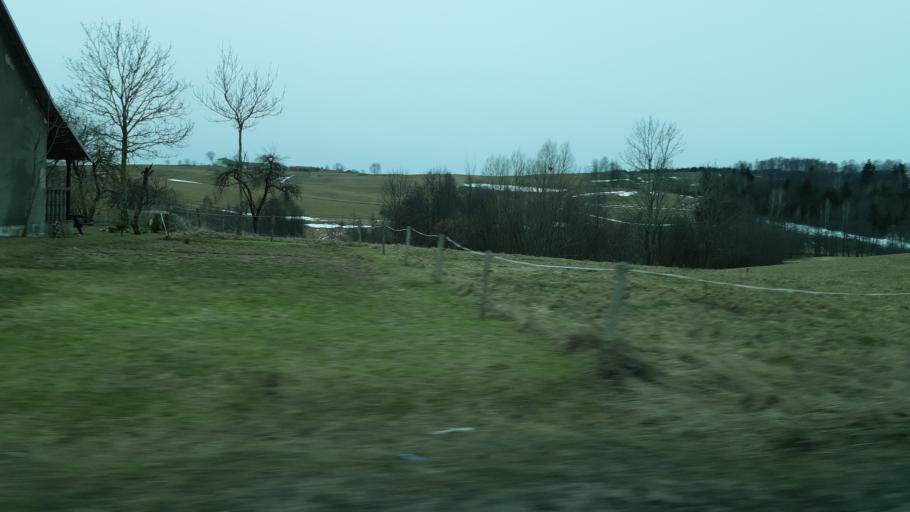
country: PL
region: Podlasie
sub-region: Suwalki
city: Suwalki
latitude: 54.3324
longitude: 22.9427
